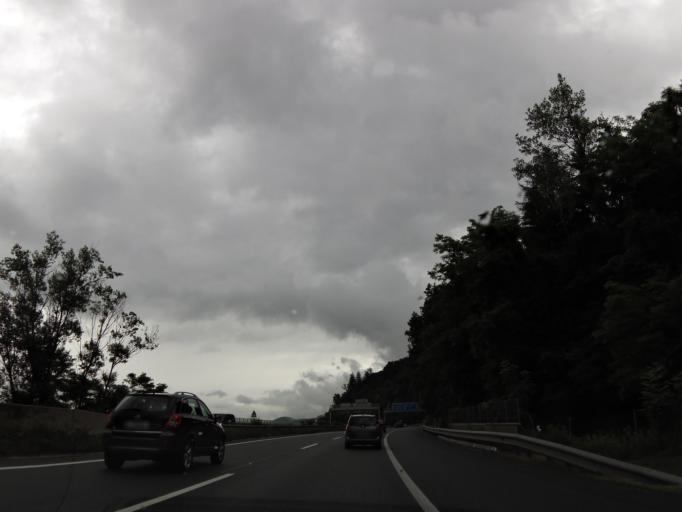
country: AT
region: Tyrol
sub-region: Innsbruck Stadt
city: Innsbruck
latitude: 47.2536
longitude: 11.3802
